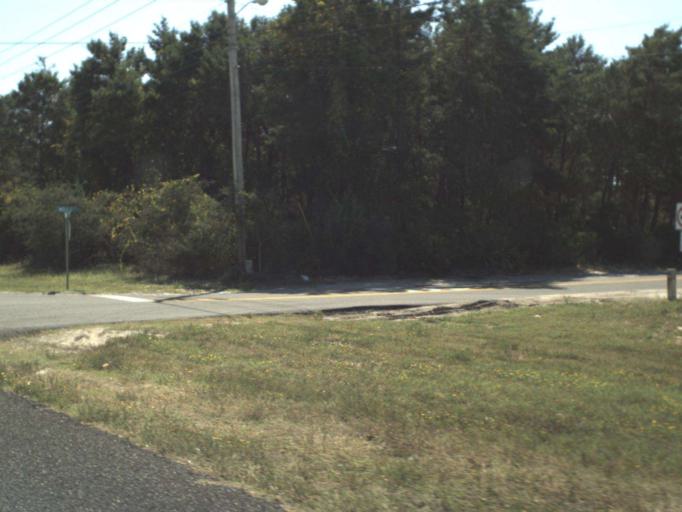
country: US
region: Florida
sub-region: Bay County
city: Laguna Beach
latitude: 30.2408
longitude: -85.9140
